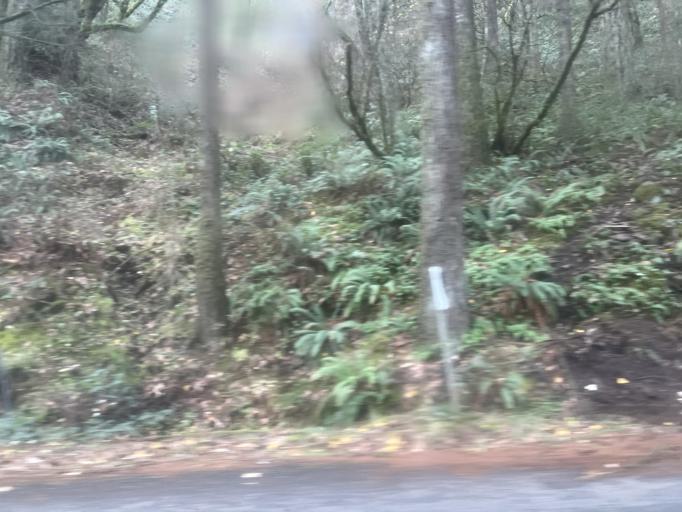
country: US
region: Washington
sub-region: Clark County
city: Washougal
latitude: 45.5489
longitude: -122.1938
